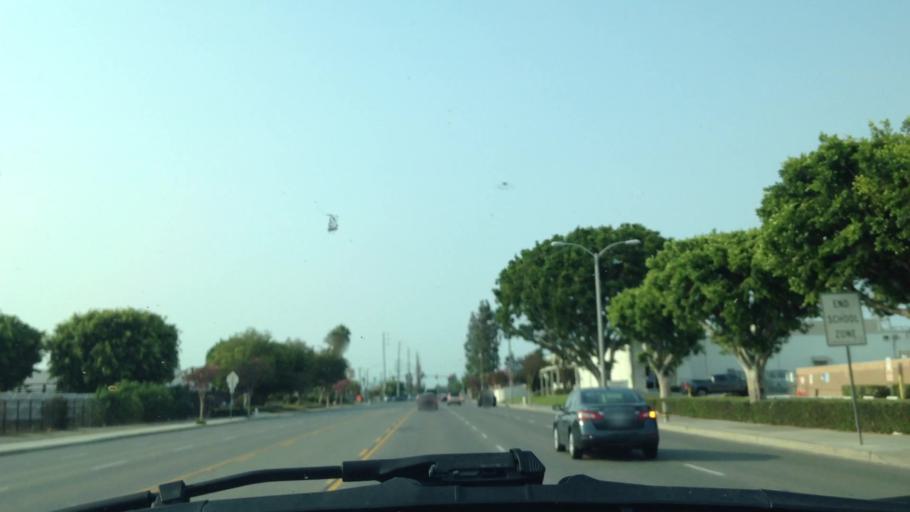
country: US
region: California
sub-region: Orange County
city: Santa Ana
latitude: 33.7311
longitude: -117.8504
